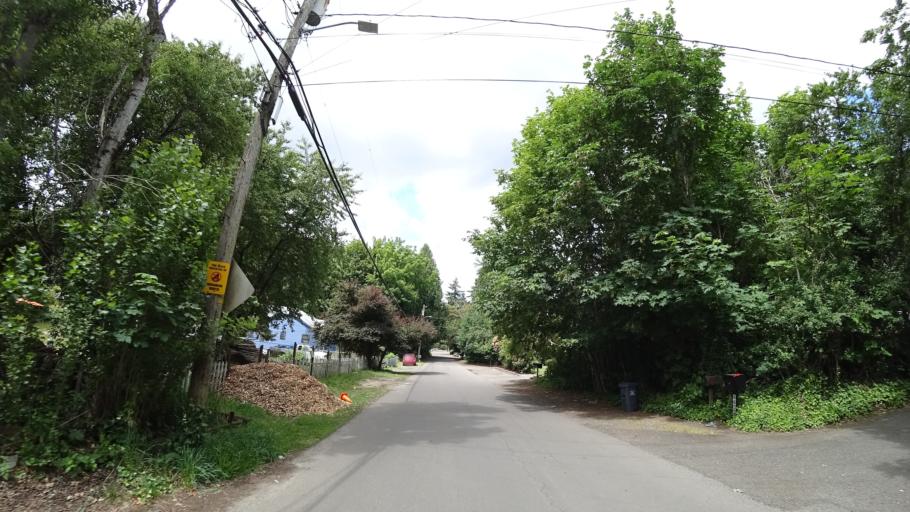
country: US
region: Oregon
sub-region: Multnomah County
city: Portland
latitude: 45.5686
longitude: -122.6172
